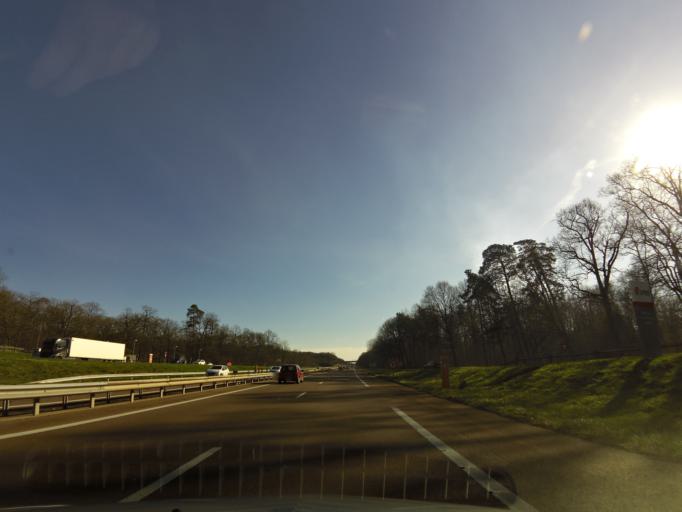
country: FR
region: Bourgogne
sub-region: Departement de l'Yonne
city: Moneteau
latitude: 47.8453
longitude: 3.6087
